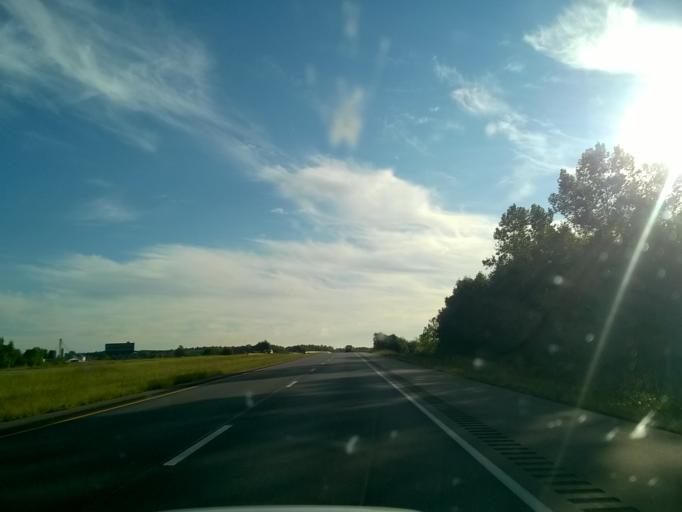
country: US
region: Indiana
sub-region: Warrick County
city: Chandler
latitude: 38.1893
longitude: -87.3498
